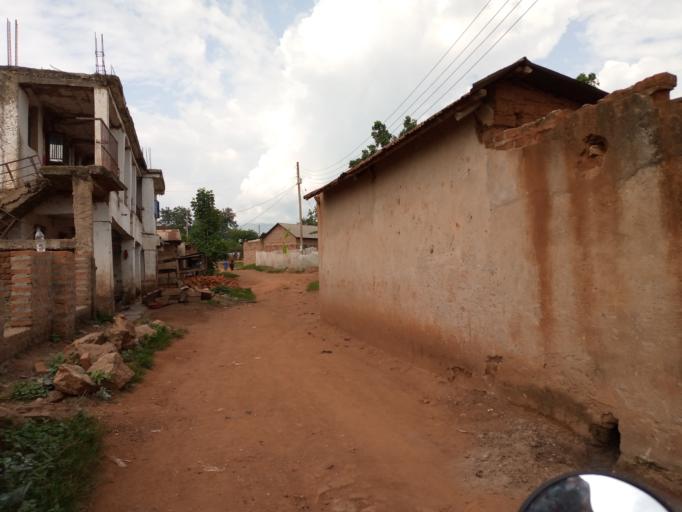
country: UG
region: Eastern Region
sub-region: Mbale District
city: Mbale
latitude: 1.0817
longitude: 34.1652
